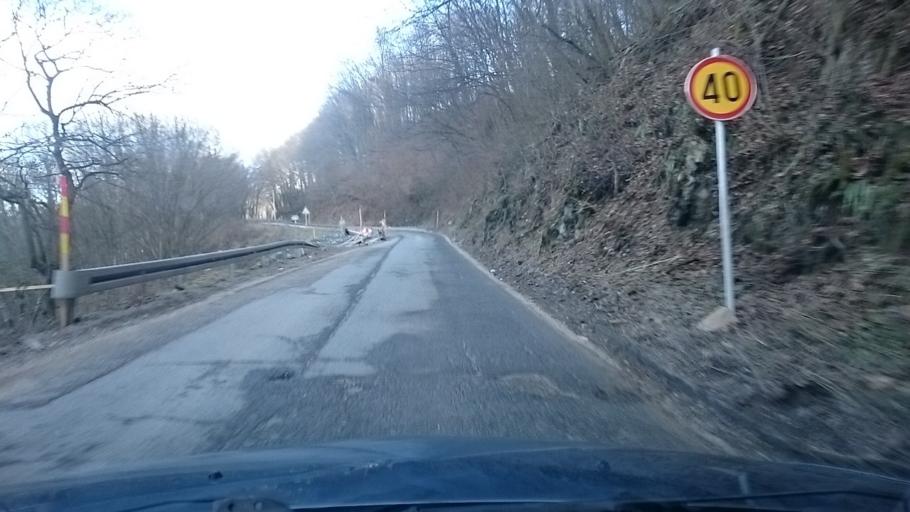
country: BA
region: Republika Srpska
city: Starcevica
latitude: 44.6867
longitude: 17.2057
